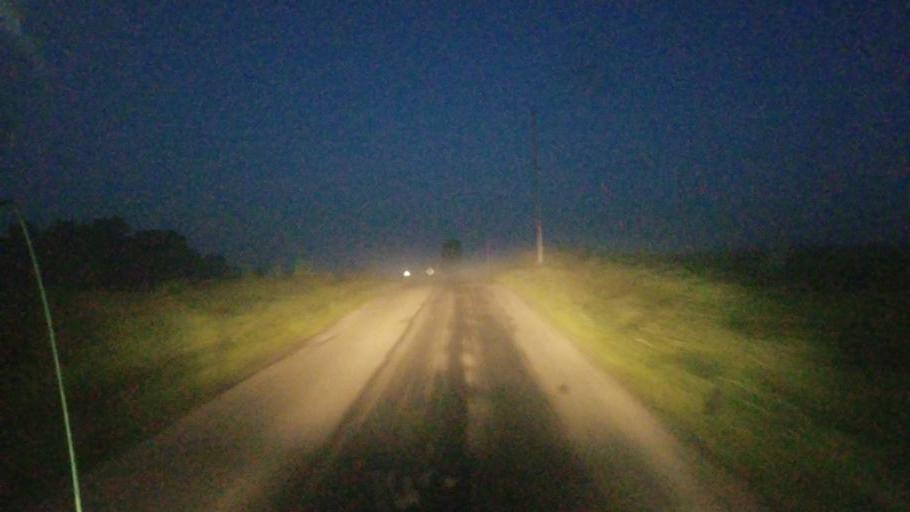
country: US
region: Ohio
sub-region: Perry County
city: Thornport
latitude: 39.9181
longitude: -82.3384
